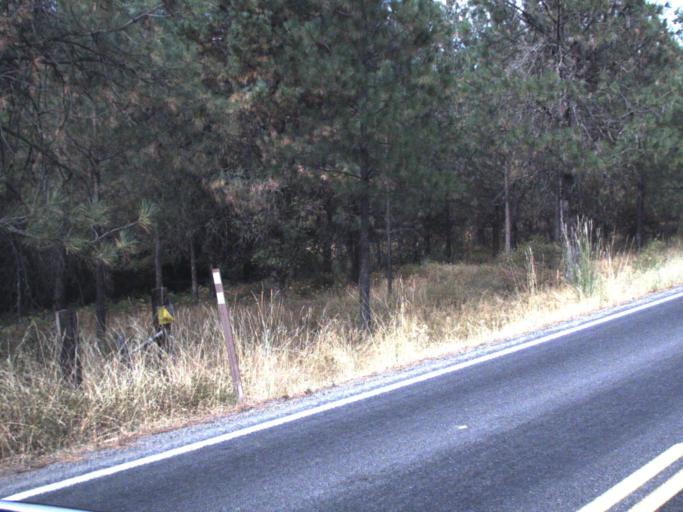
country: US
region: Washington
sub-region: Spokane County
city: Trentwood
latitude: 47.8281
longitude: -117.2055
